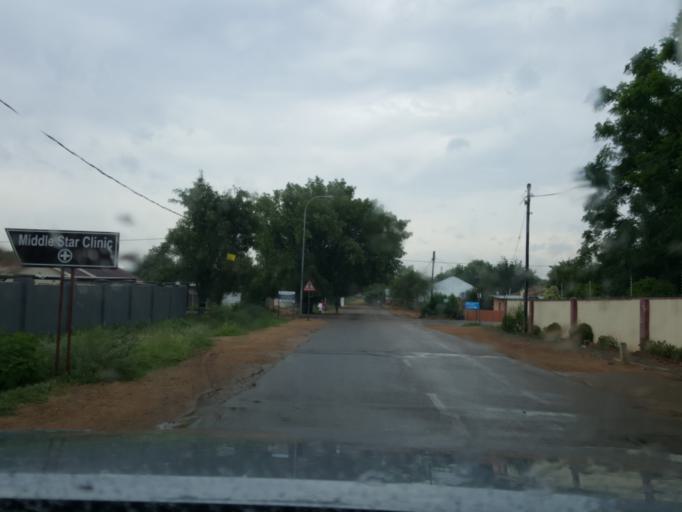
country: BW
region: South East
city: Gaborone
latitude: -24.6422
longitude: 25.9210
